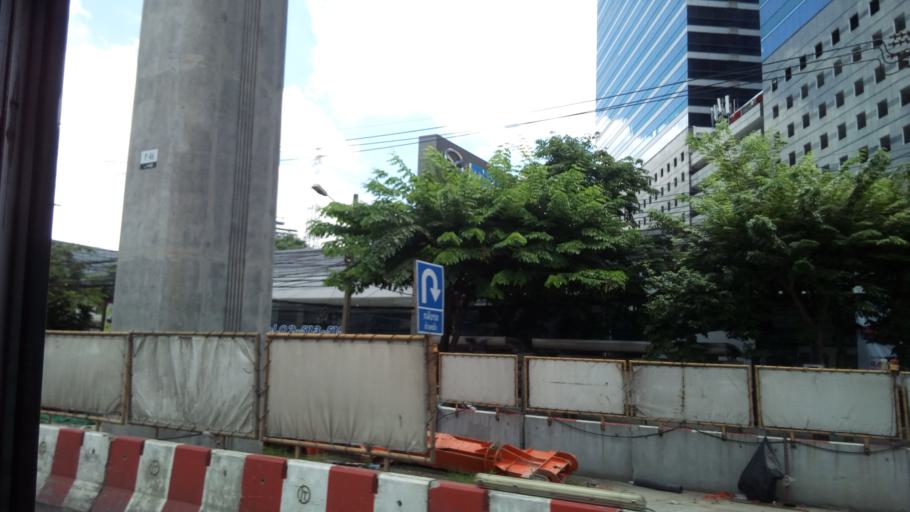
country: TH
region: Bangkok
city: Chatuchak
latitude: 13.8197
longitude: 100.5639
